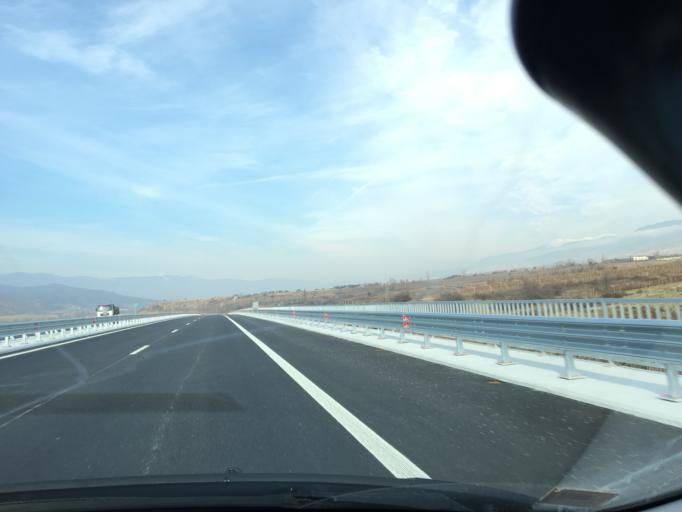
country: BG
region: Blagoevgrad
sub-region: Obshtina Sandanski
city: Sandanski
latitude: 41.5479
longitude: 23.2530
